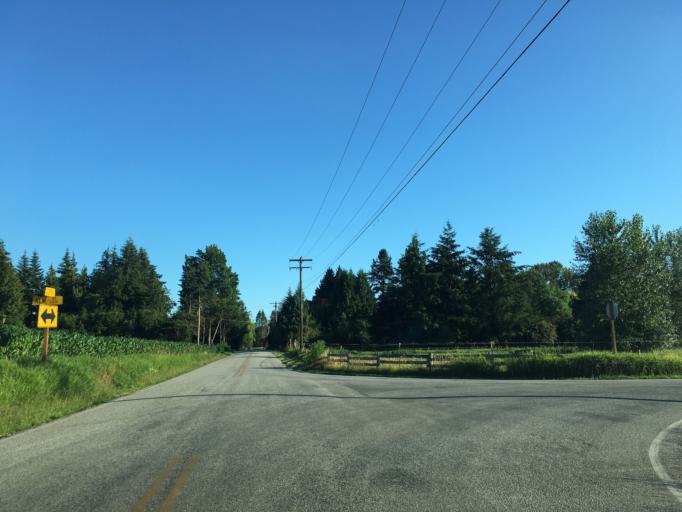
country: US
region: Washington
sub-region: Whatcom County
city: Nooksack
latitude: 48.9440
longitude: -122.3095
